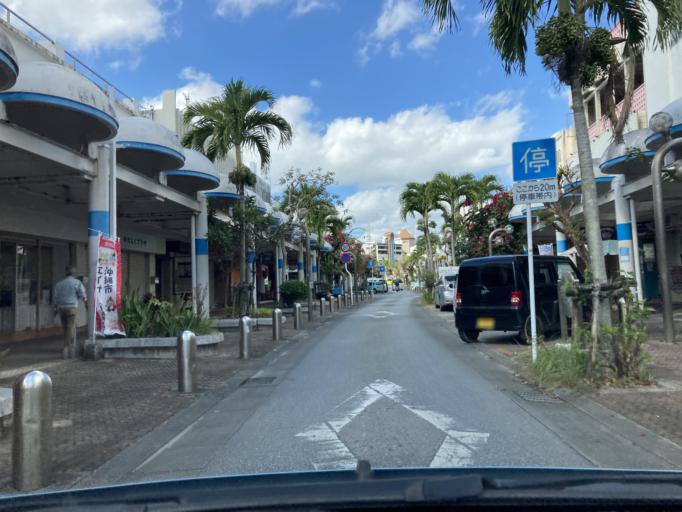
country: JP
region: Okinawa
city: Okinawa
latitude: 26.3381
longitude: 127.8012
